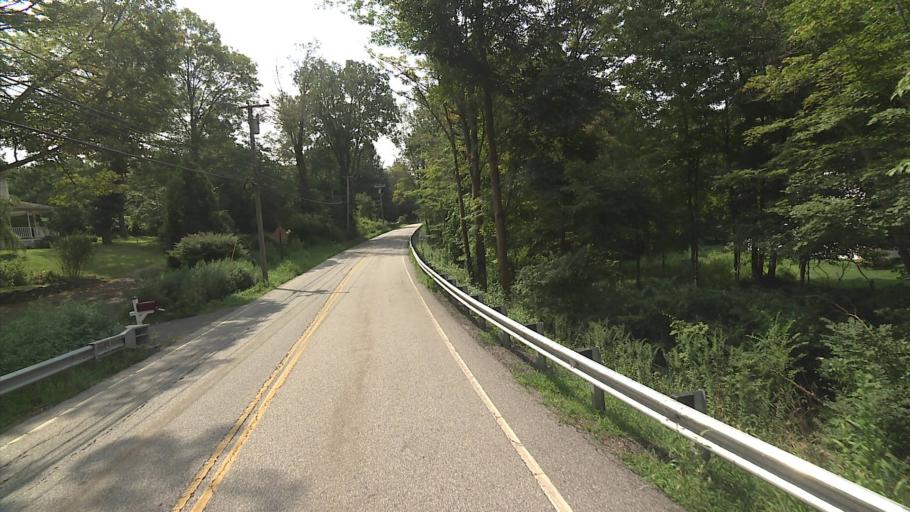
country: US
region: Connecticut
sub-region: Middlesex County
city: Chester Center
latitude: 41.4307
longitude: -72.4052
